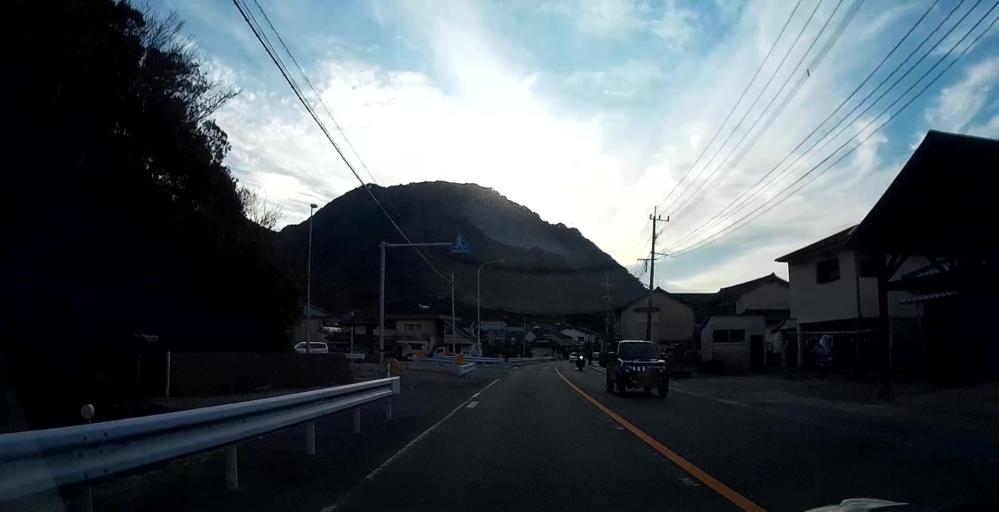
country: JP
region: Nagasaki
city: Shimabara
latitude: 32.6378
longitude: 130.4761
